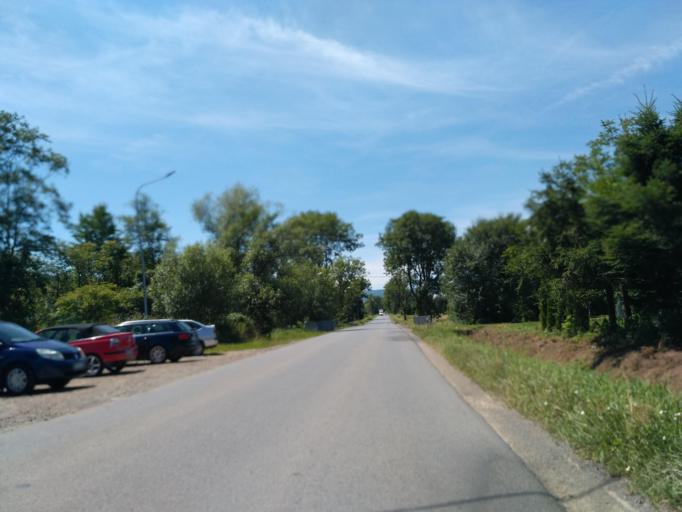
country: PL
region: Subcarpathian Voivodeship
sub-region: Powiat sanocki
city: Bukowsko
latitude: 49.5005
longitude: 22.0768
